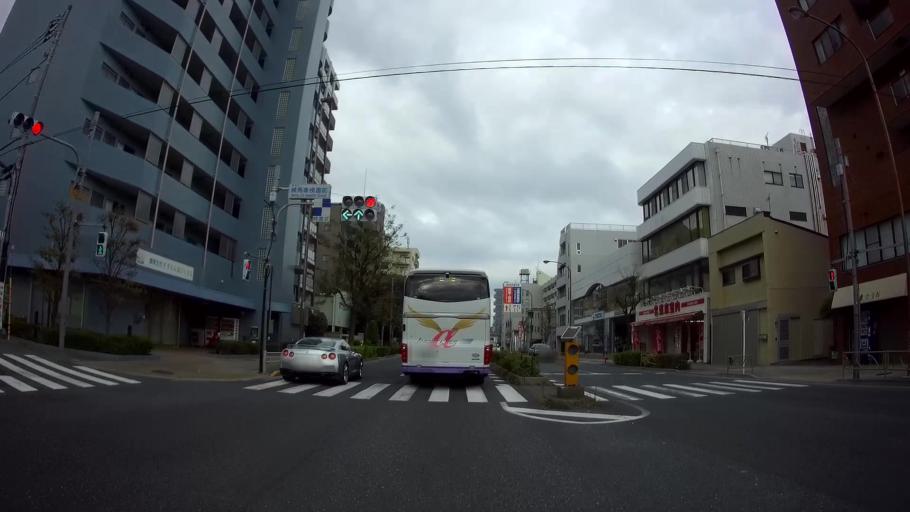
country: JP
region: Saitama
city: Wako
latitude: 35.7660
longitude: 139.6573
